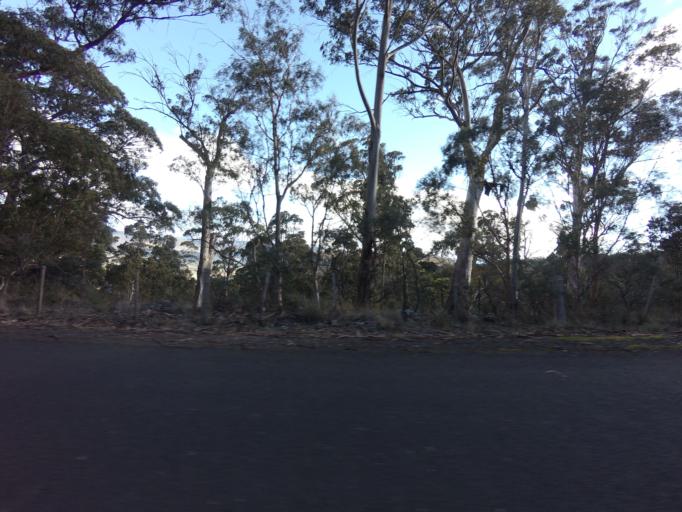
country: AU
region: Tasmania
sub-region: Derwent Valley
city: New Norfolk
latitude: -42.7289
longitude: 147.0314
